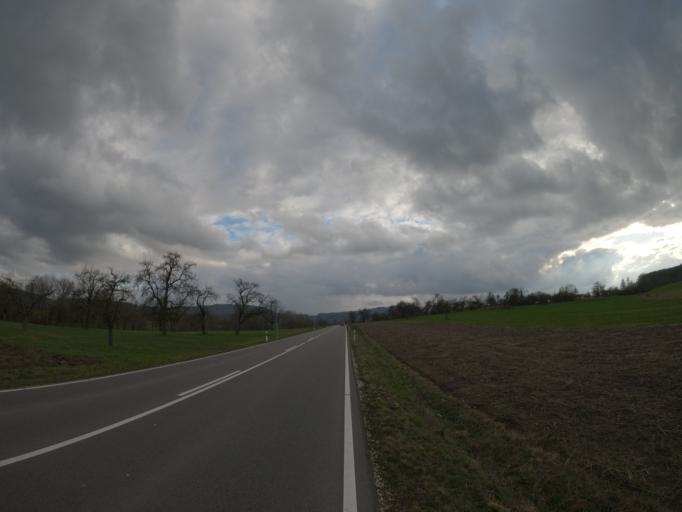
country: DE
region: Baden-Wuerttemberg
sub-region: Regierungsbezirk Stuttgart
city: Boll
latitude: 48.6607
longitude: 9.6144
